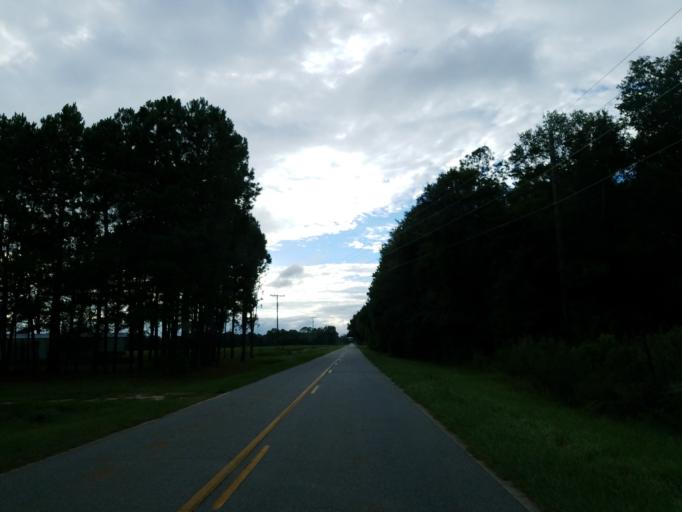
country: US
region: Georgia
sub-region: Cook County
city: Sparks
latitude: 31.2174
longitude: -83.4683
